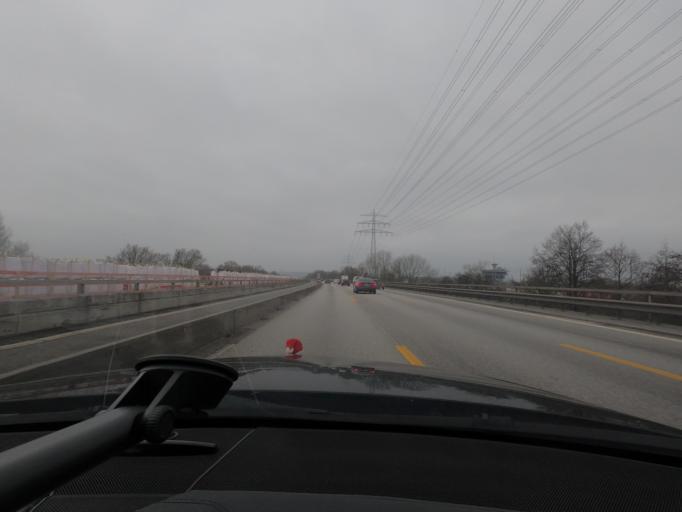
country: DE
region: Hamburg
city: Altona
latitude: 53.5069
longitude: 9.9120
